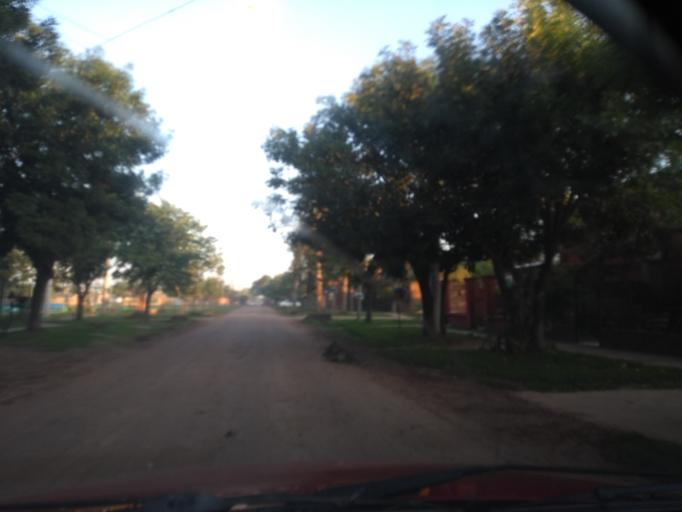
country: AR
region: Chaco
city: Resistencia
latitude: -27.4529
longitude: -58.9633
